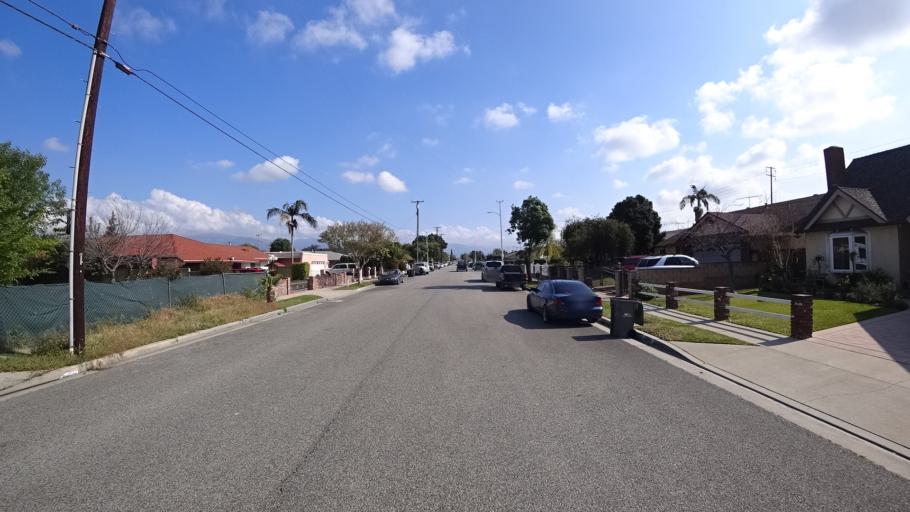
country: US
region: California
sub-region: Los Angeles County
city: Baldwin Park
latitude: 34.0782
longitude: -117.9606
